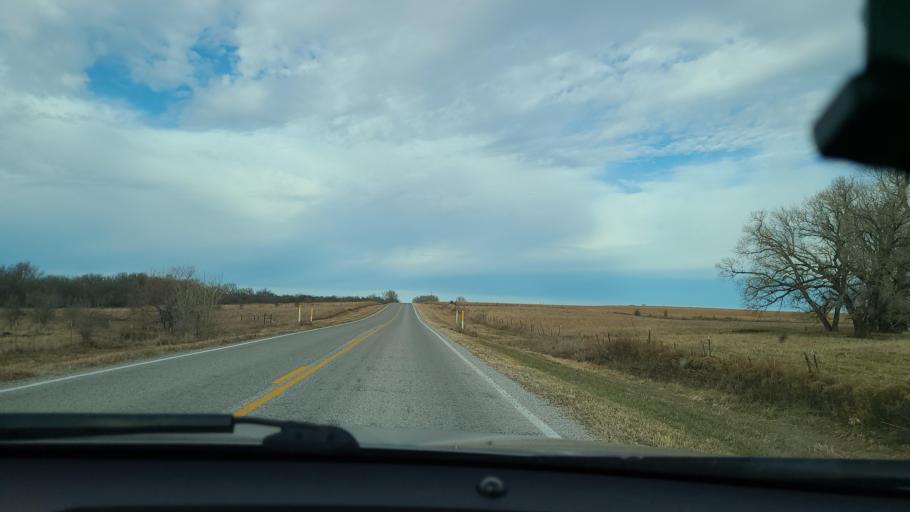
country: US
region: Kansas
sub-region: McPherson County
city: Inman
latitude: 38.3390
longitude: -97.9245
